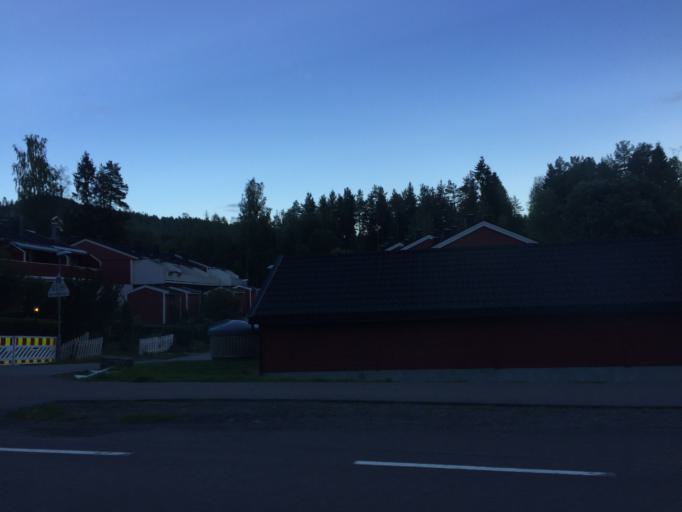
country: NO
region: Akershus
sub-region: Skedsmo
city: Lillestrom
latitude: 59.9330
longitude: 11.0275
